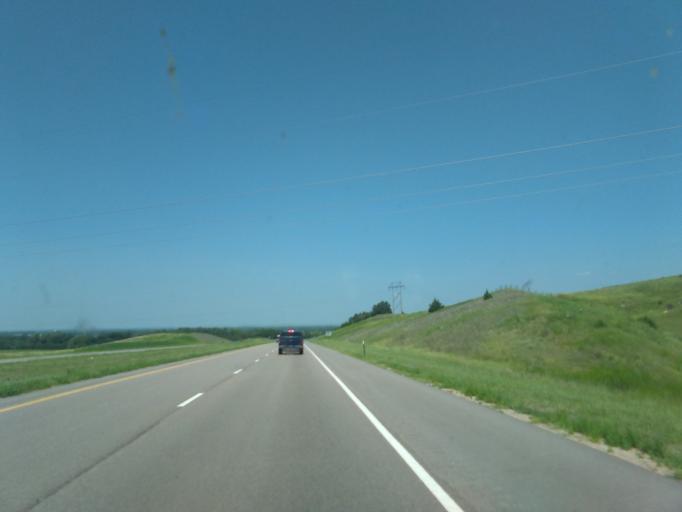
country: US
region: Nebraska
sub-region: Lincoln County
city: North Platte
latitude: 41.0777
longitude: -100.7630
